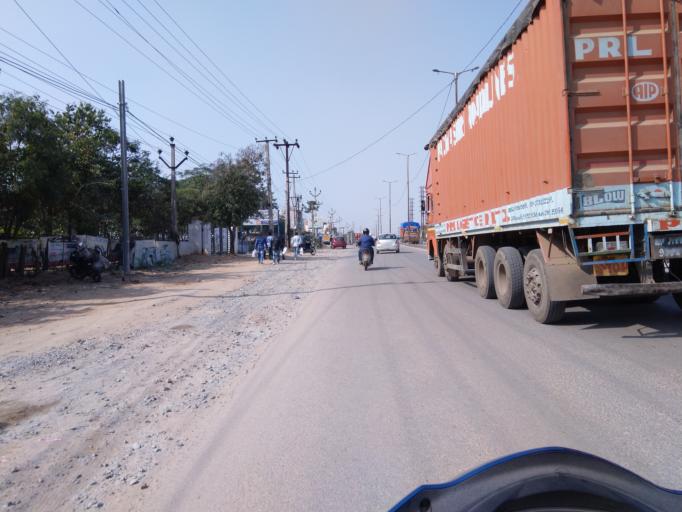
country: IN
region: Telangana
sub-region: Rangareddi
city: Quthbullapur
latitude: 17.5347
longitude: 78.4351
